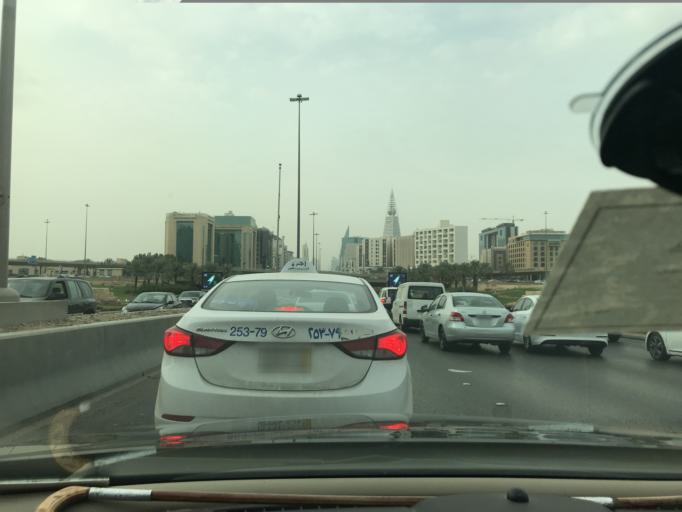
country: SA
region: Ar Riyad
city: Riyadh
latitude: 24.6769
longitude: 46.6898
